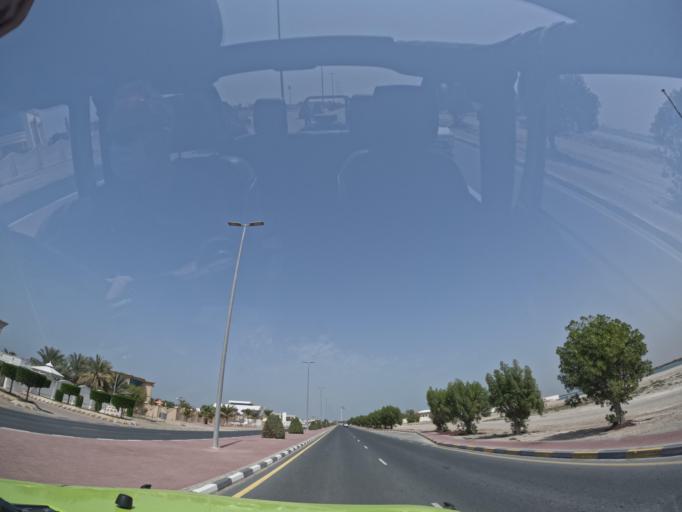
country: AE
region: Umm al Qaywayn
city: Umm al Qaywayn
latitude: 25.5510
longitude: 55.5596
